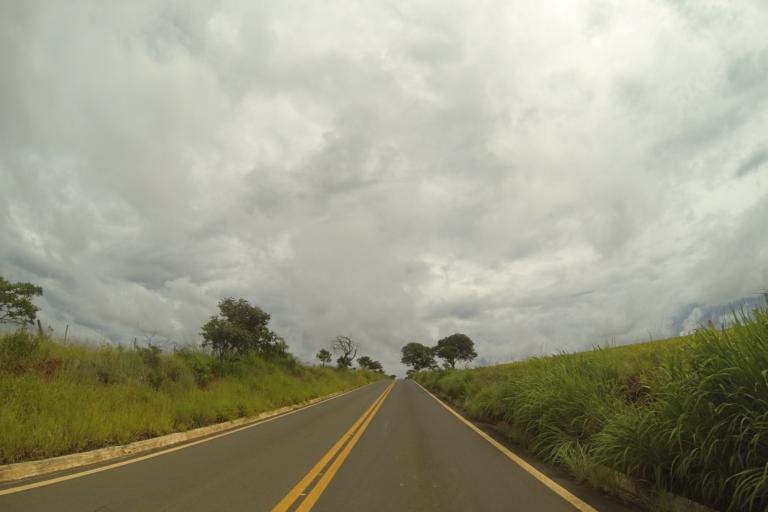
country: BR
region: Minas Gerais
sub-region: Bambui
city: Bambui
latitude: -20.1017
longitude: -46.1168
